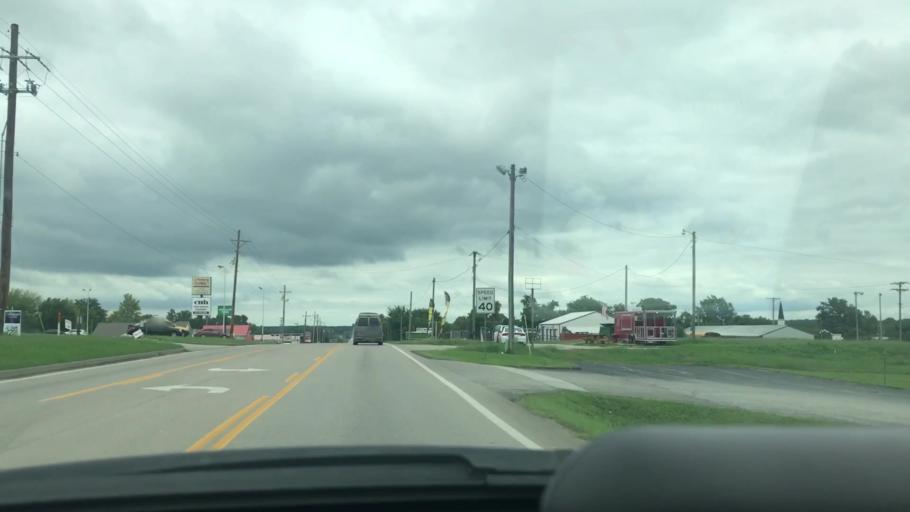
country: US
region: Missouri
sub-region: Dallas County
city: Buffalo
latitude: 37.6413
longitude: -93.1042
